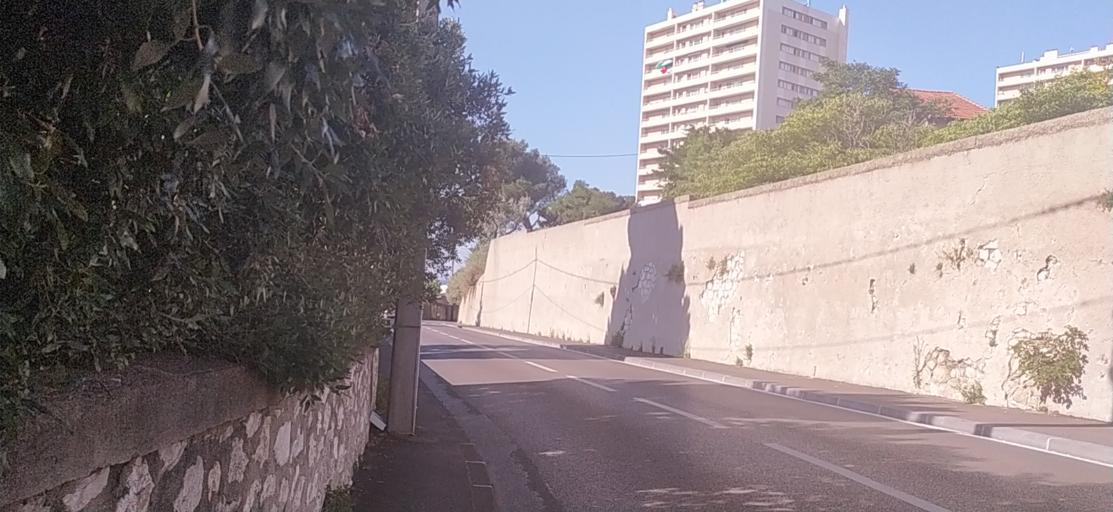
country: FR
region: Provence-Alpes-Cote d'Azur
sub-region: Departement des Bouches-du-Rhone
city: Marseille 16
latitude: 43.3401
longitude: 5.3521
